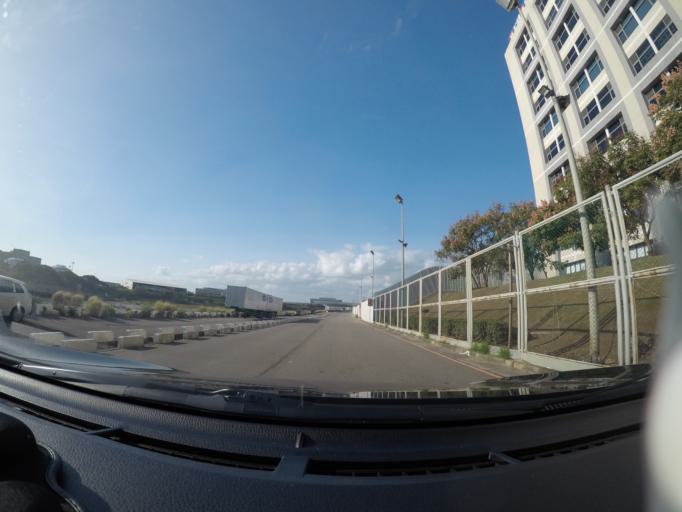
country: TW
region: Taiwan
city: Taoyuan City
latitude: 25.0932
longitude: 121.2530
